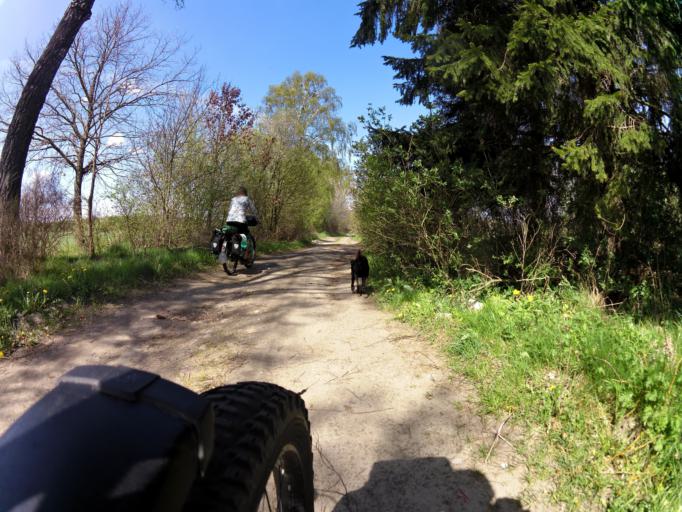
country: PL
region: West Pomeranian Voivodeship
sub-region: Powiat lobeski
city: Resko
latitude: 53.8023
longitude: 15.4442
